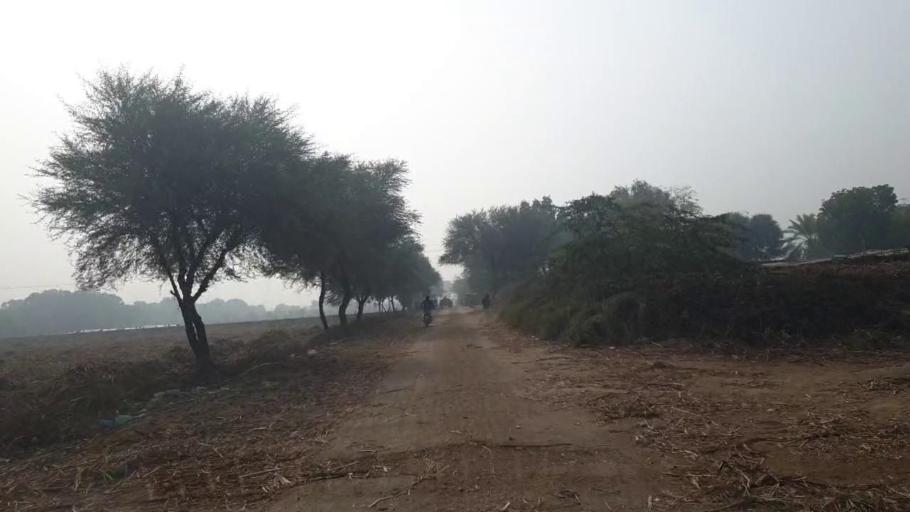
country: PK
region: Sindh
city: Tando Adam
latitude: 25.7689
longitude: 68.6073
